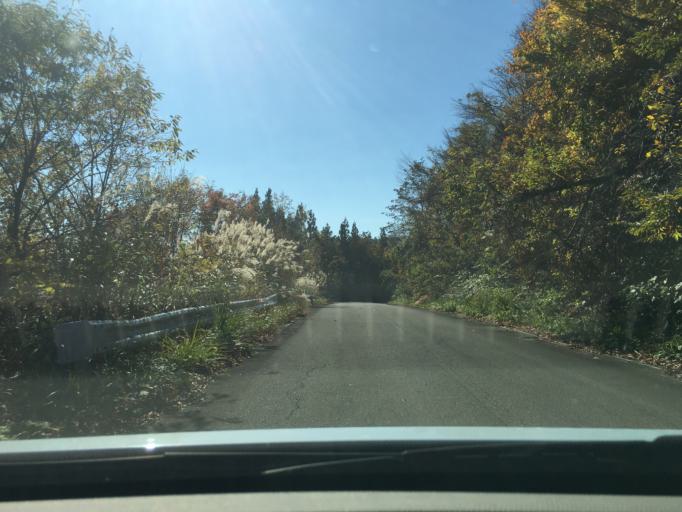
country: JP
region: Fukushima
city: Inawashiro
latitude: 37.4017
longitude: 140.0243
